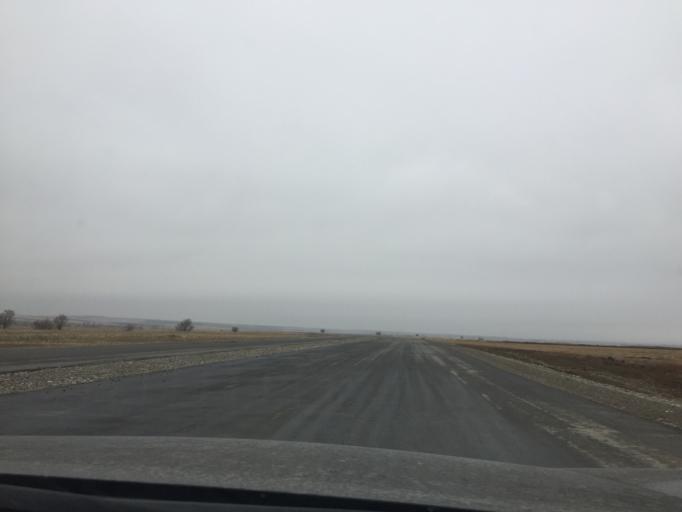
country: KZ
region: Ongtustik Qazaqstan
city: Turar Ryskulov
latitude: 42.5188
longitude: 70.3247
